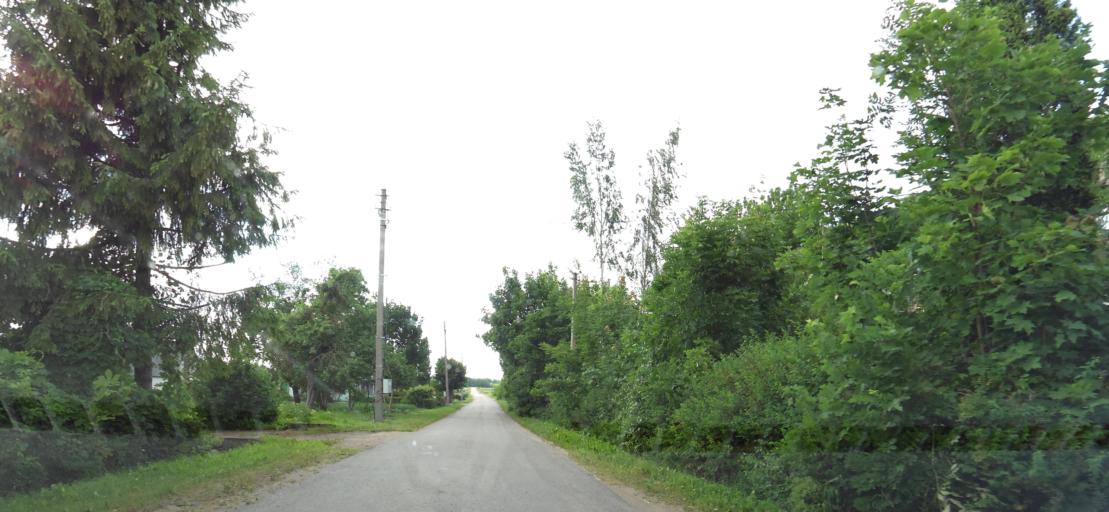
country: LT
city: Obeliai
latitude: 55.8990
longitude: 25.1921
